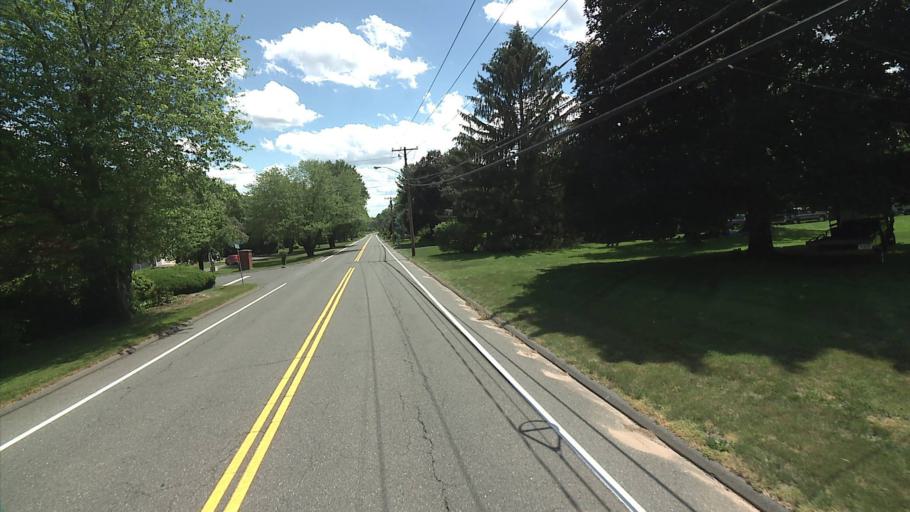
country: US
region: Connecticut
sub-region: Tolland County
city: Somers
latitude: 42.0159
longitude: -72.4835
